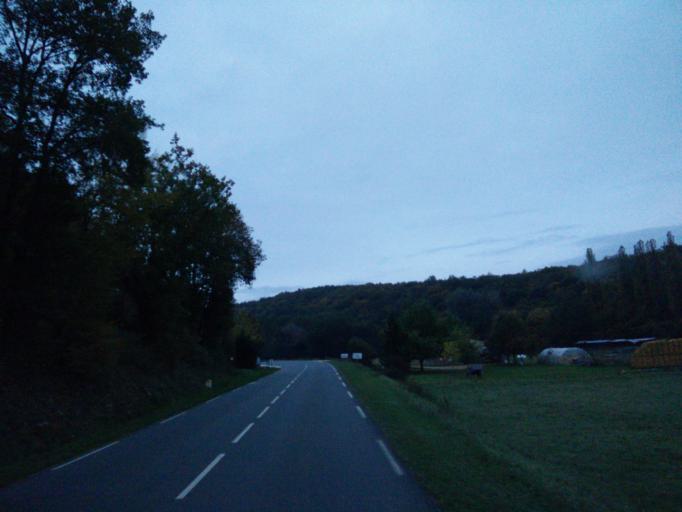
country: FR
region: Aquitaine
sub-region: Departement de la Dordogne
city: Saint-Cyprien
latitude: 44.9159
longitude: 1.1080
